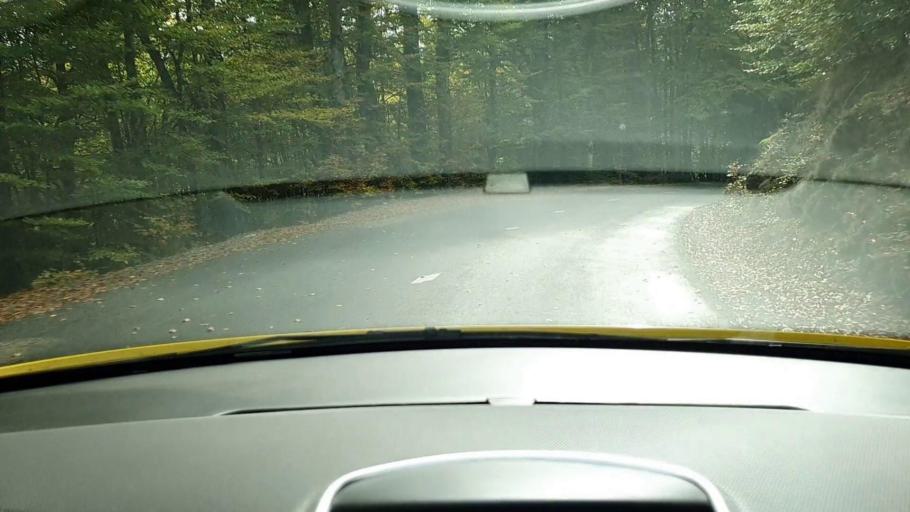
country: FR
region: Languedoc-Roussillon
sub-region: Departement du Gard
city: Valleraugue
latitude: 44.0835
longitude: 3.5354
